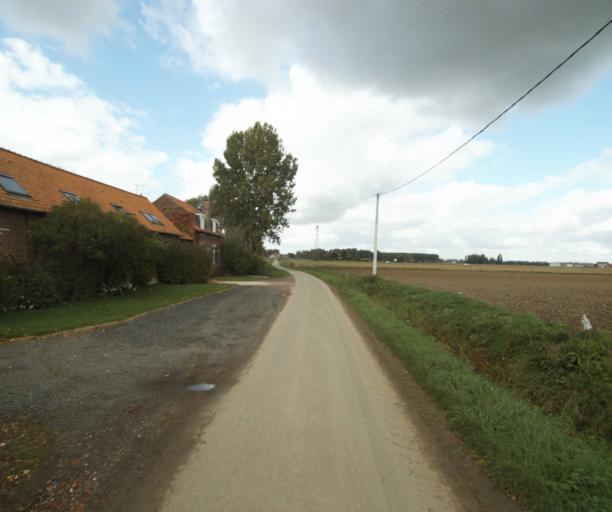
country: FR
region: Nord-Pas-de-Calais
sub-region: Departement du Nord
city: Frelinghien
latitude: 50.7078
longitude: 2.9451
